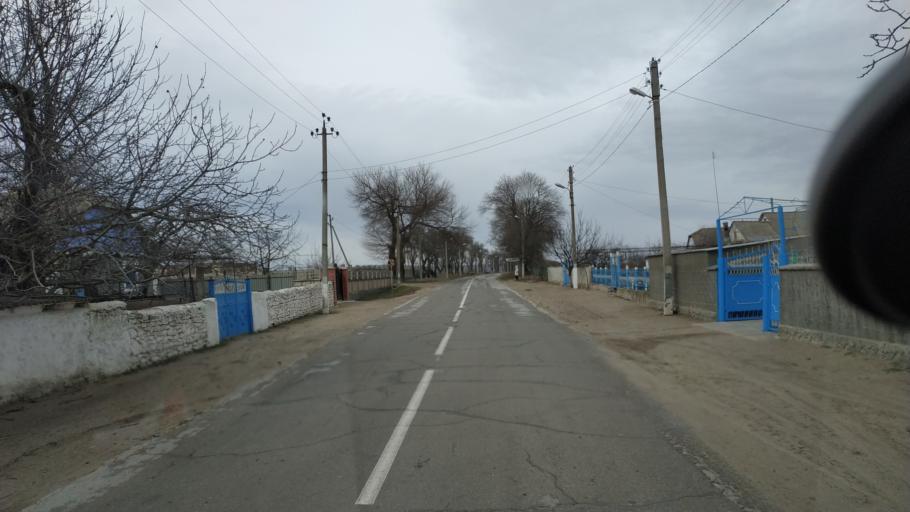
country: MD
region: Telenesti
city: Cocieri
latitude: 47.3172
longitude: 29.1032
